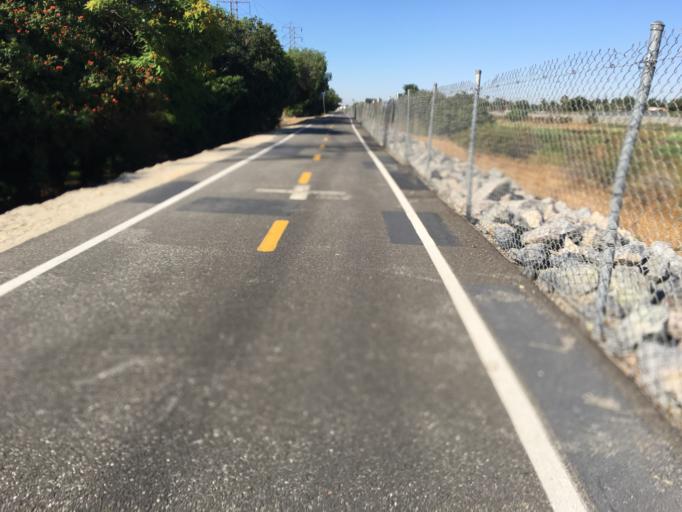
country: US
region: California
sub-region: Los Angeles County
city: Santa Fe Springs
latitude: 33.9373
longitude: -118.1015
